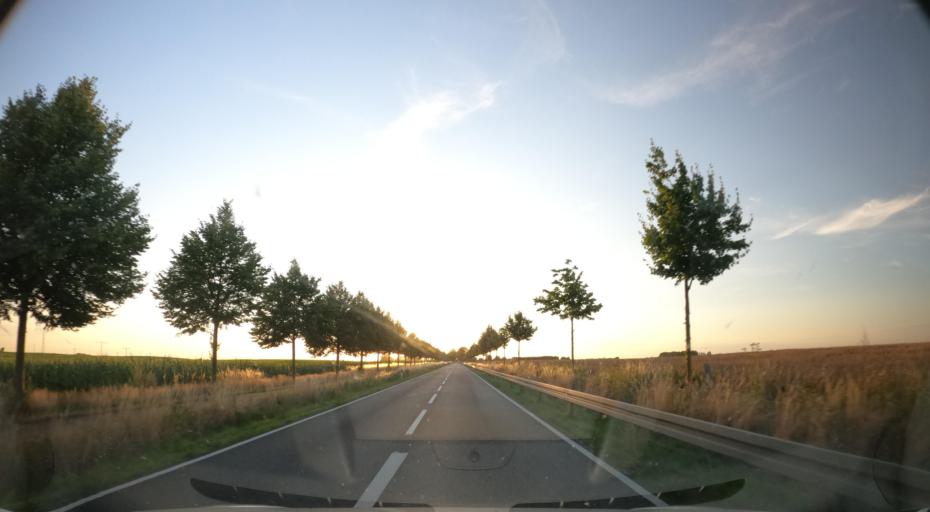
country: DE
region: Mecklenburg-Vorpommern
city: Strasburg
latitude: 53.4948
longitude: 13.7905
